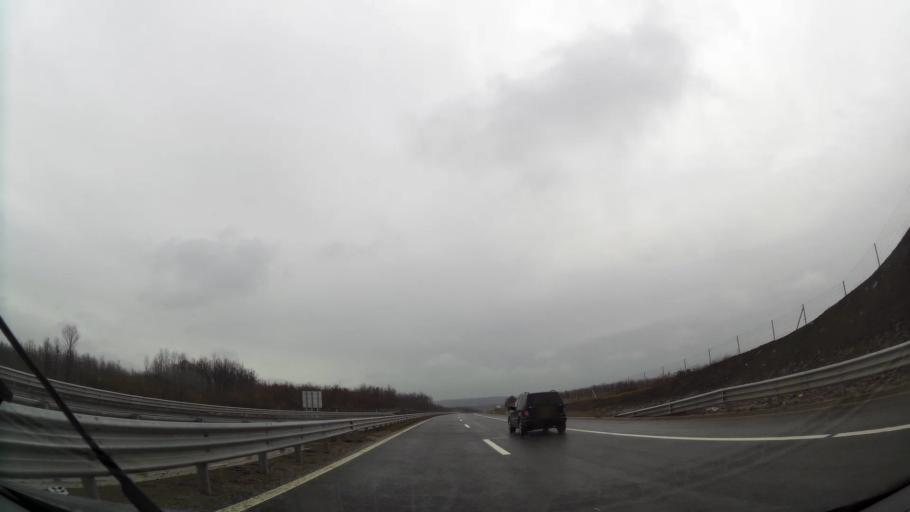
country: XK
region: Ferizaj
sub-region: Komuna e Ferizajt
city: Ferizaj
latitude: 42.3495
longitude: 21.2051
